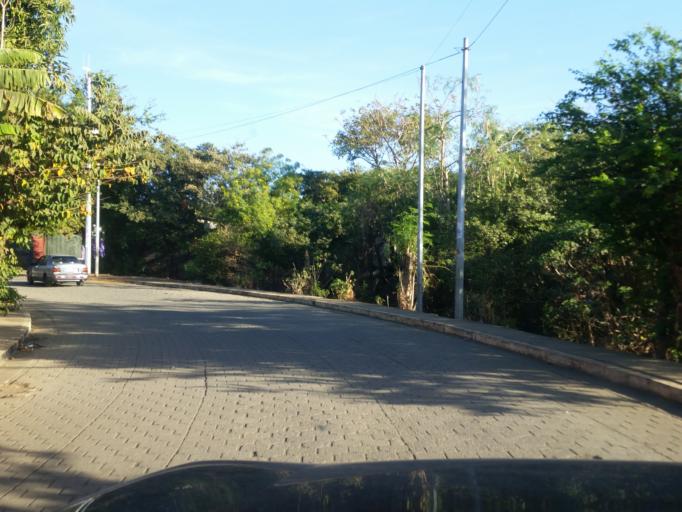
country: NI
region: Managua
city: Managua
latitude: 12.1066
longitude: -86.2402
